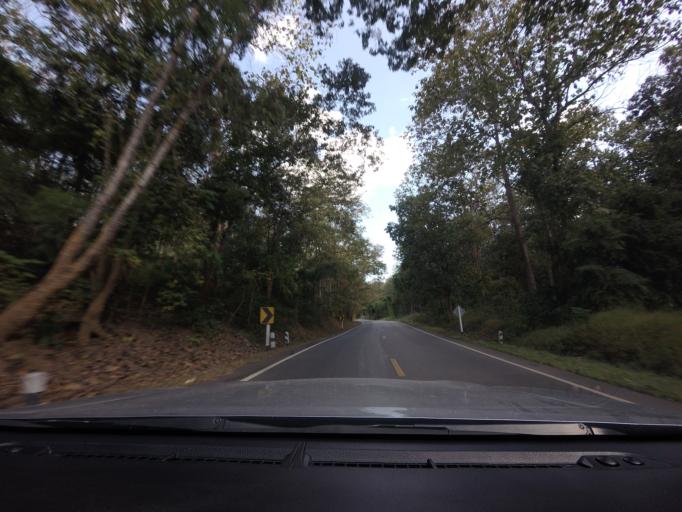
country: TH
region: Chiang Mai
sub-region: Amphoe Chiang Dao
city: Chiang Dao
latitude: 19.4741
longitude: 99.0065
